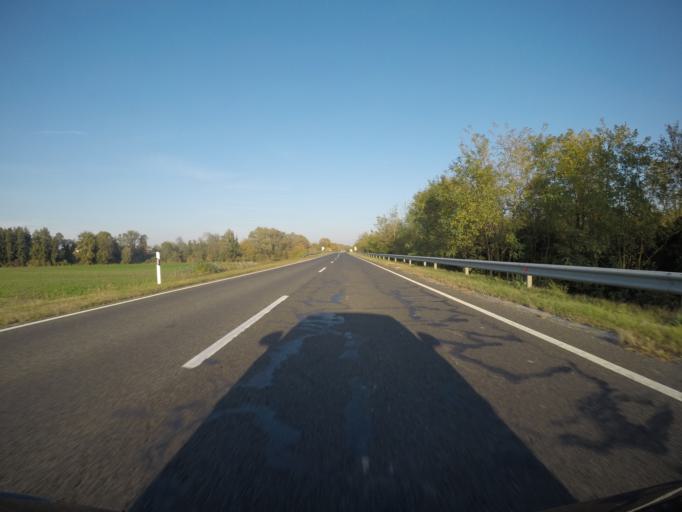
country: HU
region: Somogy
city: Barcs
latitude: 45.9566
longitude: 17.4811
